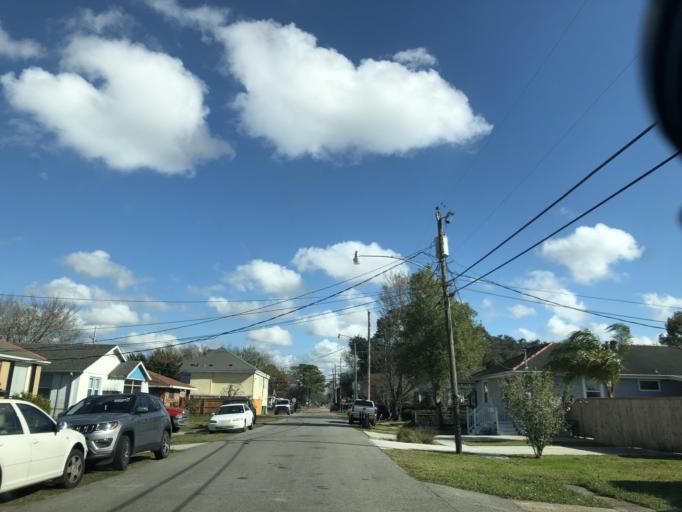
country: US
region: Louisiana
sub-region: Jefferson Parish
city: Metairie Terrace
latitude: 29.9785
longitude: -90.1684
